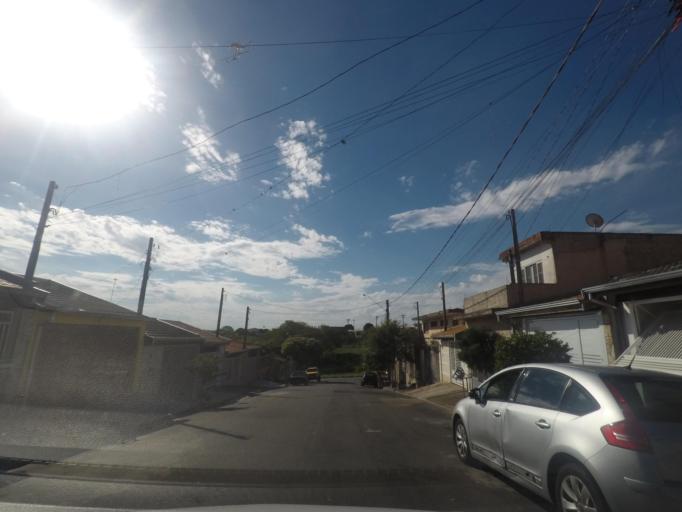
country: BR
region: Sao Paulo
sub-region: Sumare
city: Sumare
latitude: -22.8094
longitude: -47.2661
